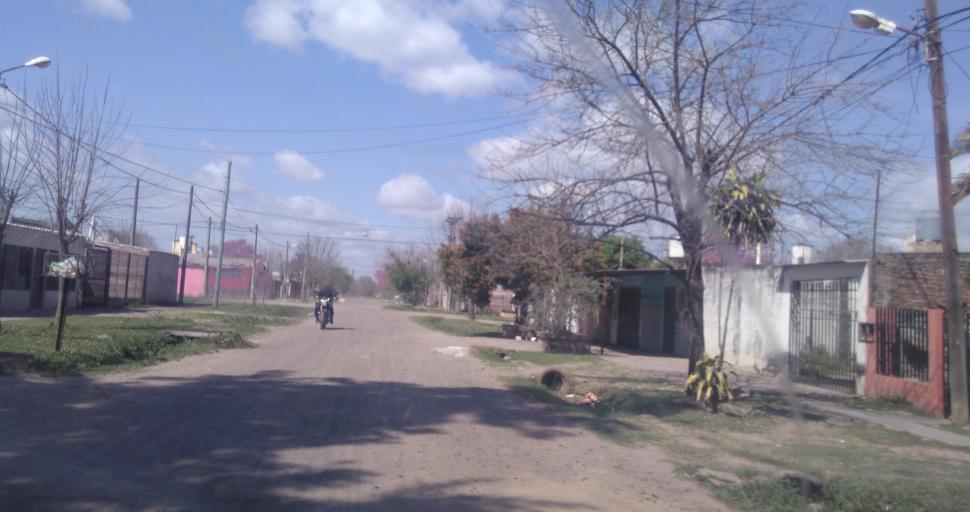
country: AR
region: Chaco
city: Fontana
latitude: -27.4307
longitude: -59.0337
